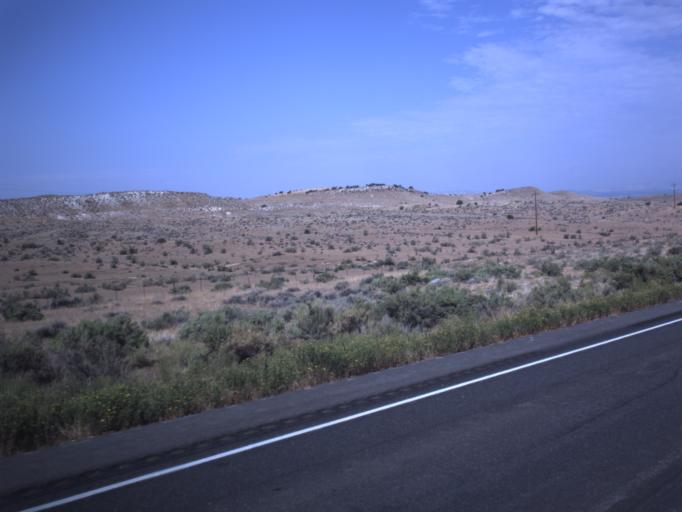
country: US
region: Utah
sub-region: Uintah County
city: Naples
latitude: 40.3361
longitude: -109.2896
